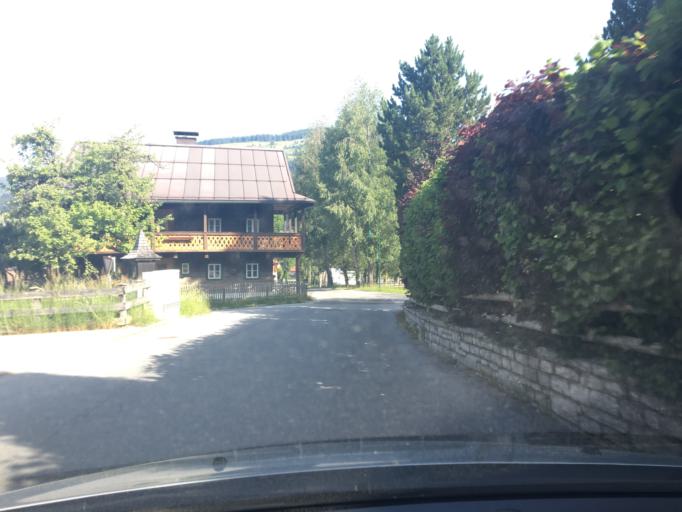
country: AT
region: Salzburg
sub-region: Politischer Bezirk Sankt Johann im Pongau
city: Wagrain
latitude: 47.3306
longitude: 13.3034
